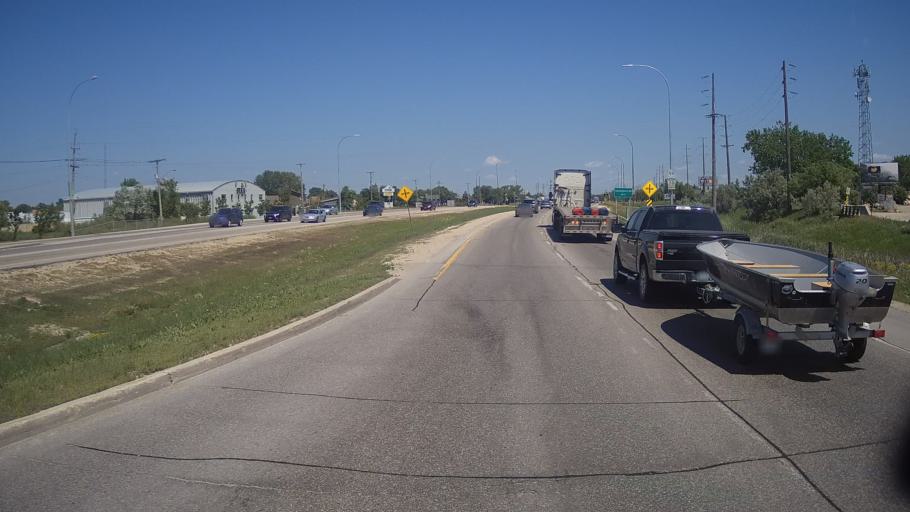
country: CA
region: Manitoba
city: Winnipeg
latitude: 49.9281
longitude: -97.0471
